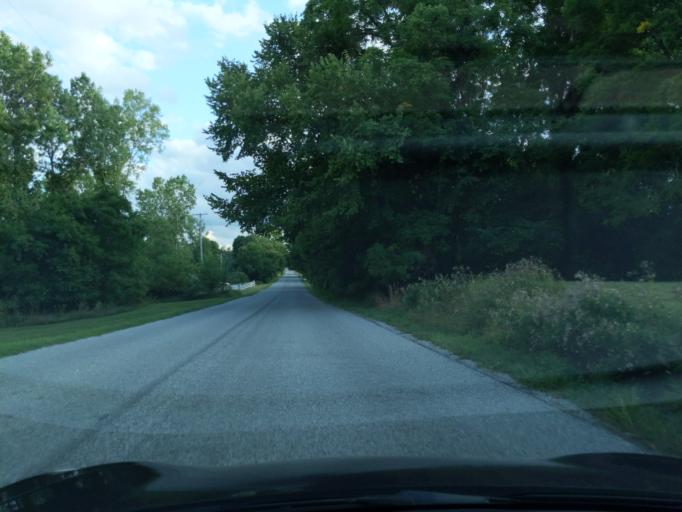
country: US
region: Michigan
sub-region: Ingham County
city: Holt
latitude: 42.6194
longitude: -84.5824
